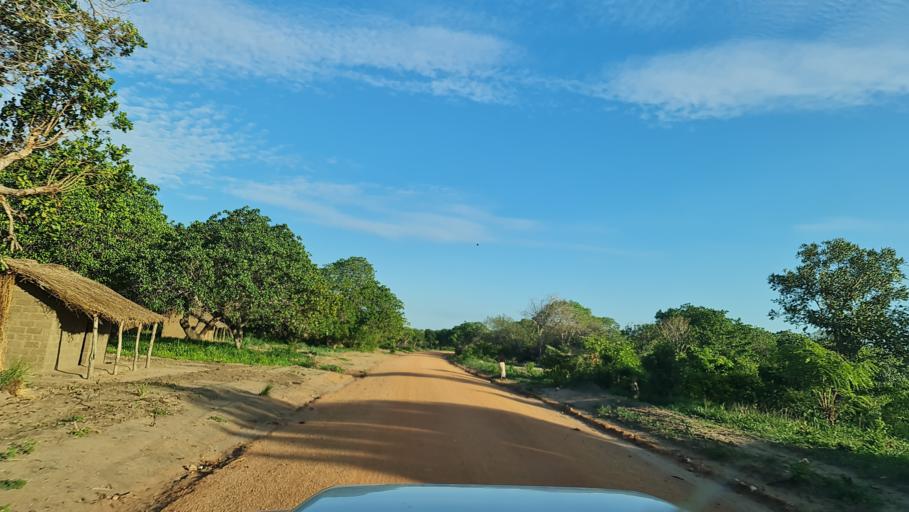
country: MZ
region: Nampula
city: Nacala
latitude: -14.6754
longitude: 40.2917
